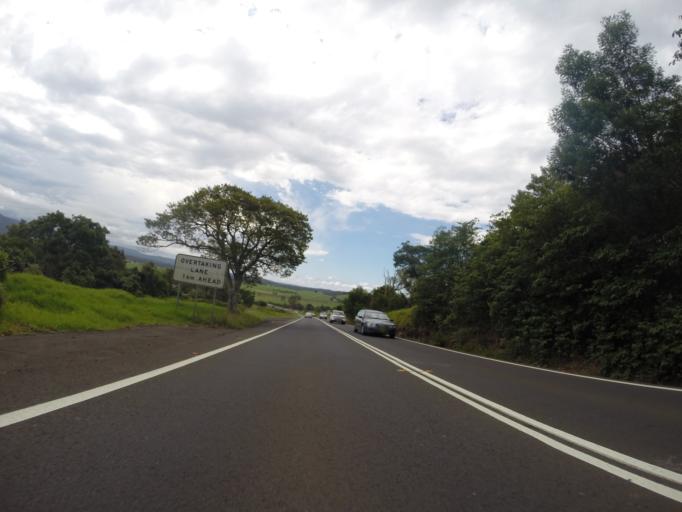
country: AU
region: New South Wales
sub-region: Shoalhaven Shire
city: Milton
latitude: -35.3070
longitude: 150.4315
